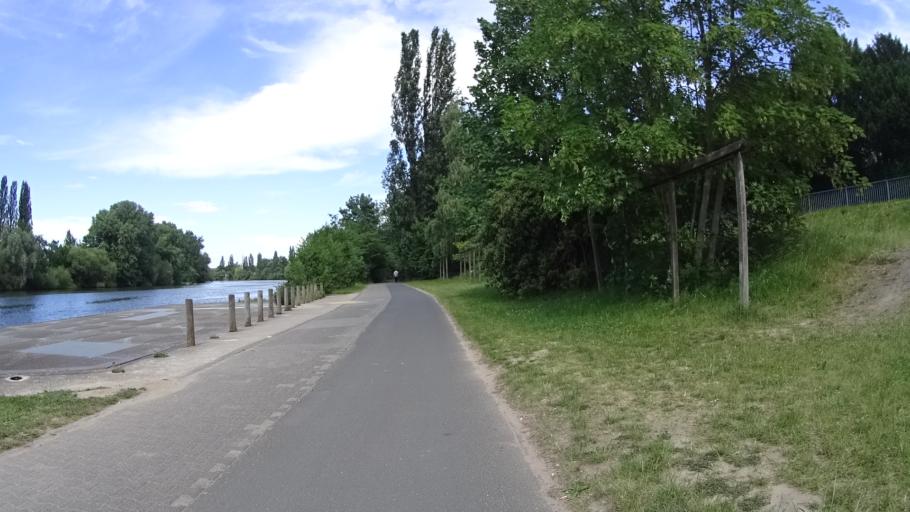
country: DE
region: Hesse
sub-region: Regierungsbezirk Darmstadt
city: Offenbach
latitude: 50.1088
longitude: 8.7771
